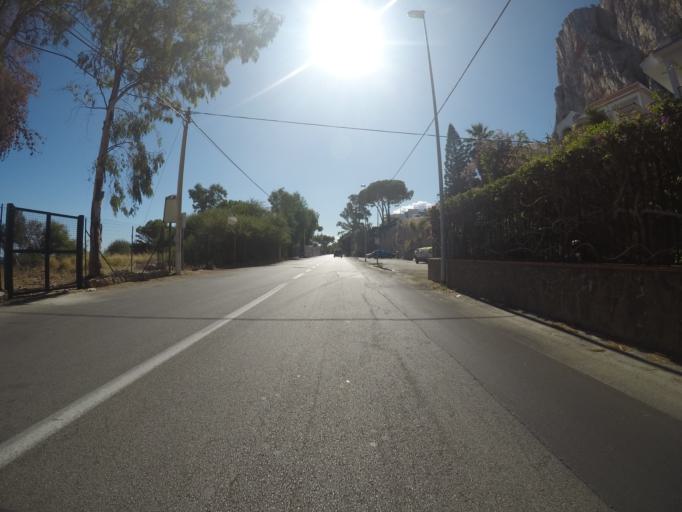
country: IT
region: Sicily
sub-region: Palermo
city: Palermo
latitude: 38.1846
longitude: 13.3629
